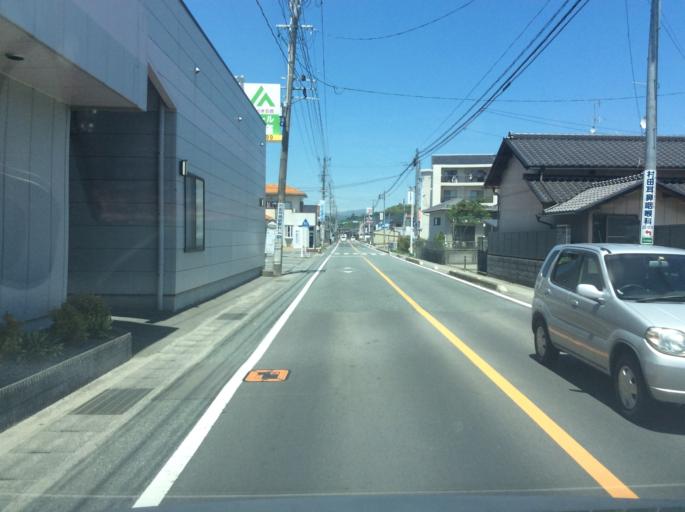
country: JP
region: Fukushima
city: Iwaki
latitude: 37.0844
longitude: 140.8779
